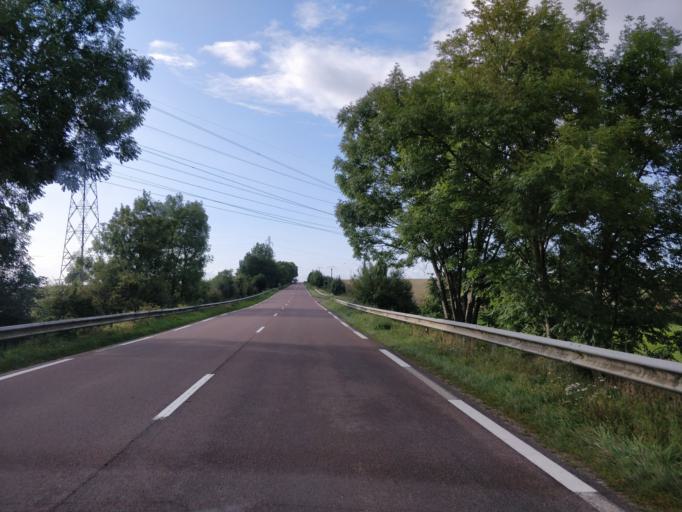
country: FR
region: Champagne-Ardenne
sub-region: Departement de l'Aube
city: Lusigny-sur-Barse
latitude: 48.2688
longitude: 4.2126
